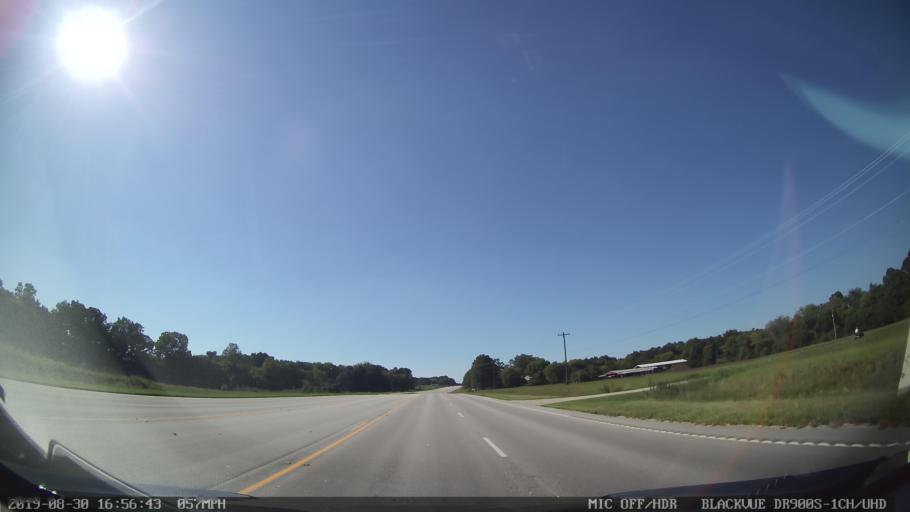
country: US
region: South Carolina
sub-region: Greenville County
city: Five Forks
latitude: 34.8067
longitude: -82.1270
